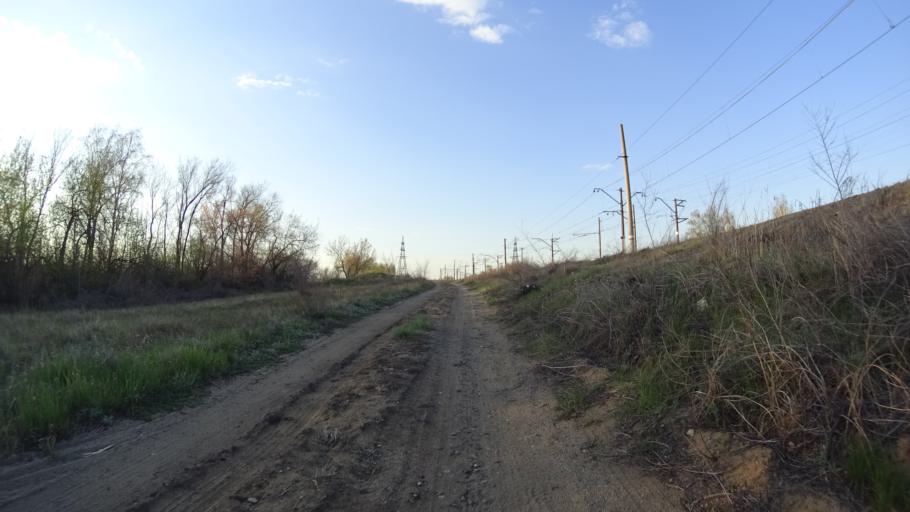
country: RU
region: Chelyabinsk
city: Troitsk
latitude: 54.0589
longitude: 61.6135
